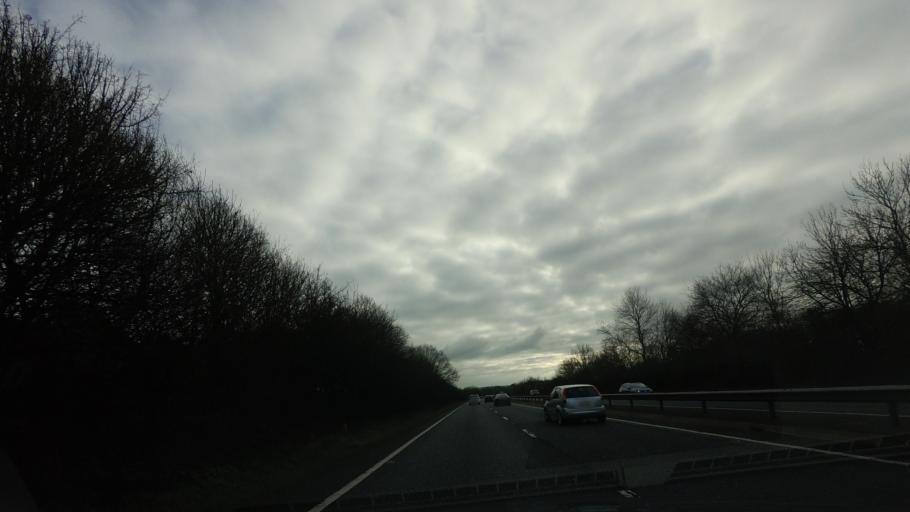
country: GB
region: England
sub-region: Kent
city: Sevenoaks
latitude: 51.2258
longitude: 0.2210
